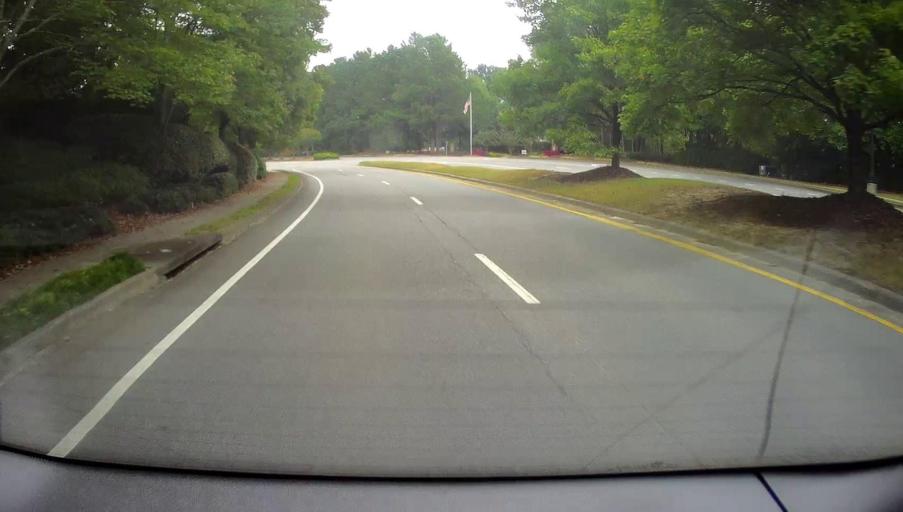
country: US
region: Georgia
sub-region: Fulton County
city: Alpharetta
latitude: 34.1037
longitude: -84.2655
